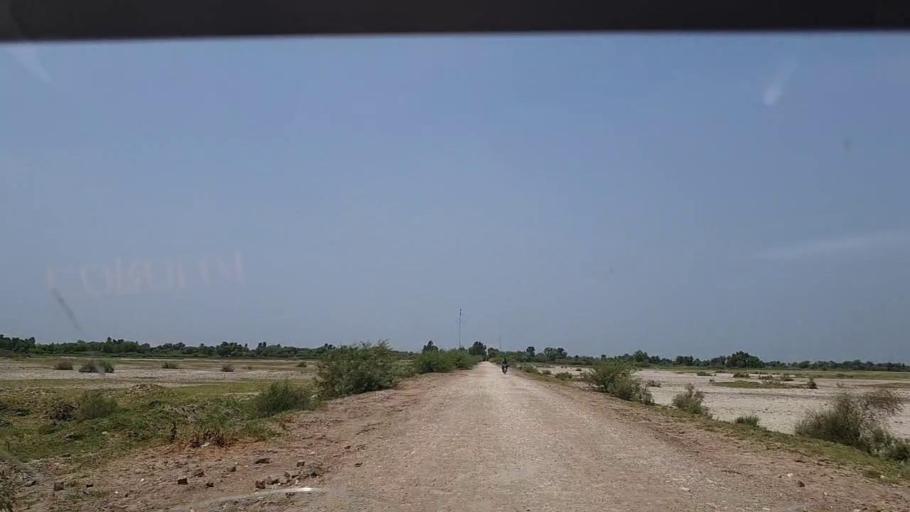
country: PK
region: Sindh
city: Adilpur
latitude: 27.9136
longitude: 69.2110
